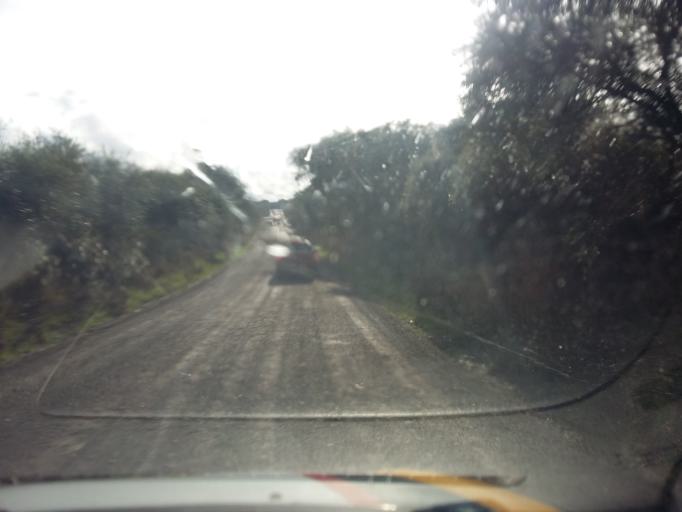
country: BR
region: Rio Grande do Sul
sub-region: Vacaria
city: Vacaria
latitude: -28.5326
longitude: -50.7982
